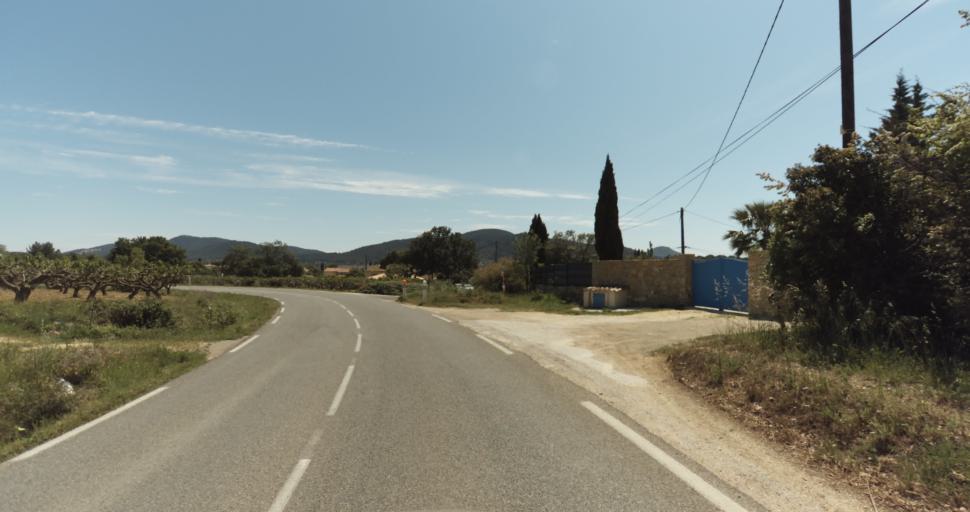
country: FR
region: Provence-Alpes-Cote d'Azur
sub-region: Departement du Var
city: La Crau
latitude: 43.1343
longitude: 6.0763
